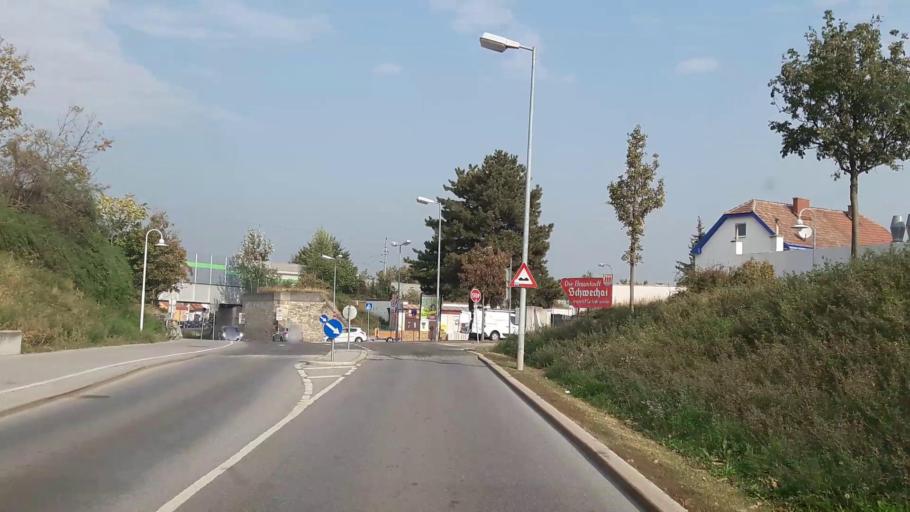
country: AT
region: Lower Austria
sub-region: Politischer Bezirk Wien-Umgebung
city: Schwechat
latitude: 48.1490
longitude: 16.4711
